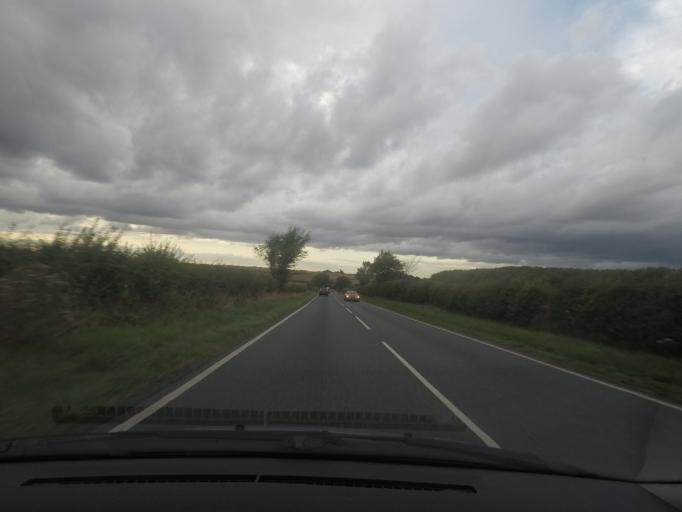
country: GB
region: England
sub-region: Lincolnshire
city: Burwell
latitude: 53.3179
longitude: 0.0119
